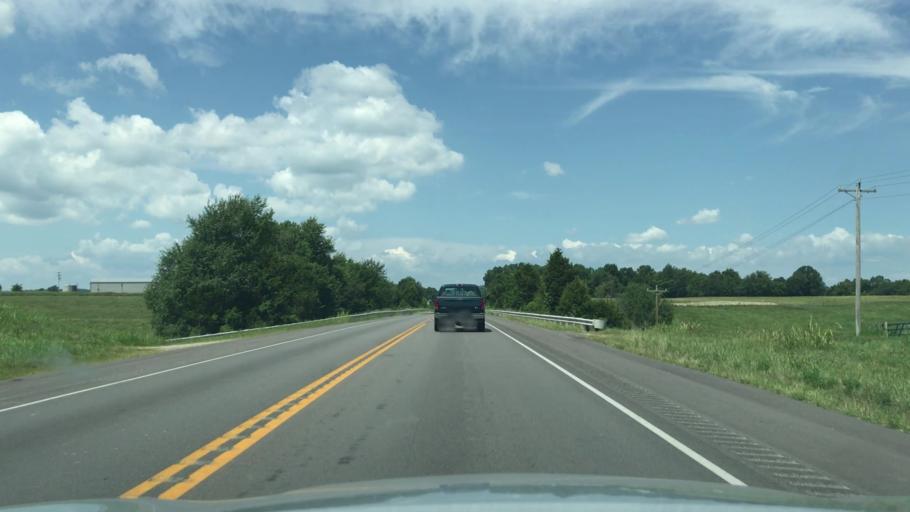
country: US
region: Kentucky
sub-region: Clinton County
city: Albany
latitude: 36.7538
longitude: -85.1242
